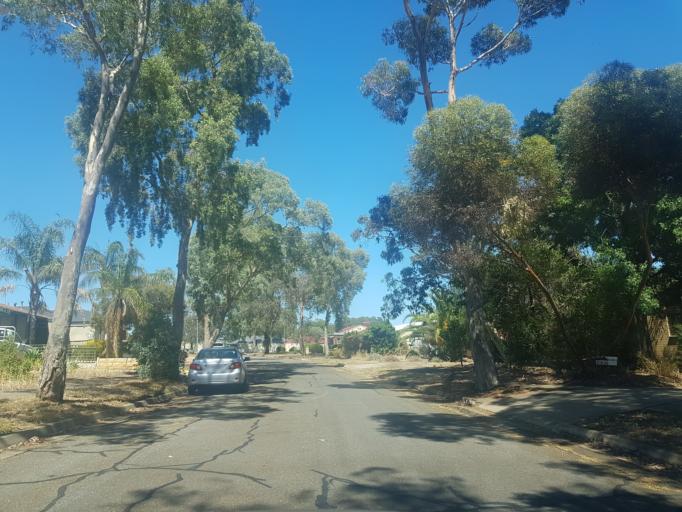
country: AU
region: South Australia
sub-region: Salisbury
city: Ingle Farm
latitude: -34.8183
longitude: 138.6432
